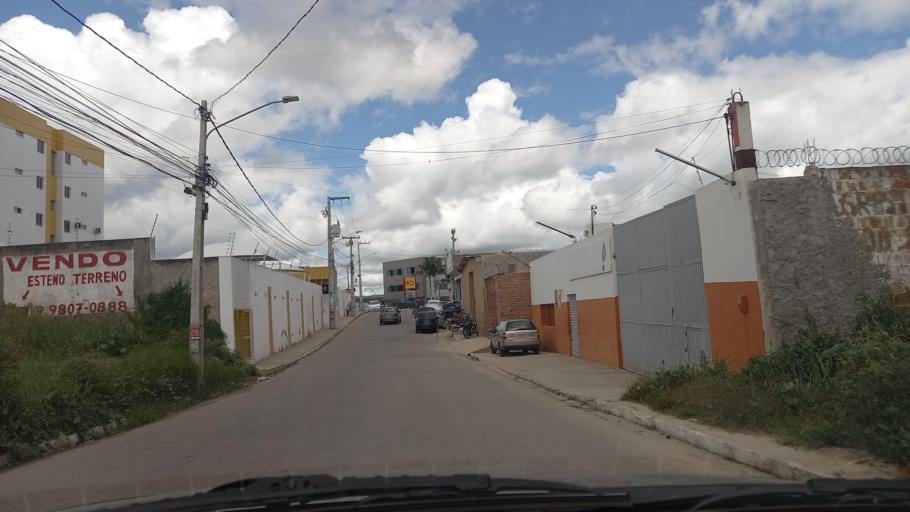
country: BR
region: Pernambuco
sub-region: Caruaru
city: Caruaru
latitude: -8.2771
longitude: -35.9411
